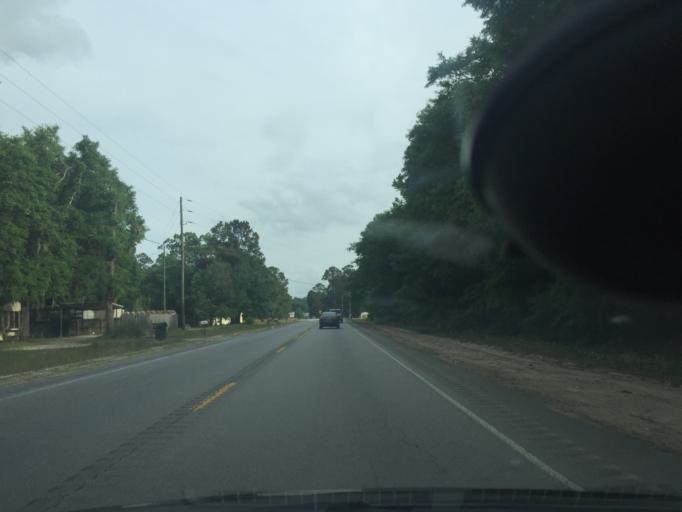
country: US
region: Georgia
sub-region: Bryan County
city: Richmond Hill
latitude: 32.0326
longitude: -81.3240
